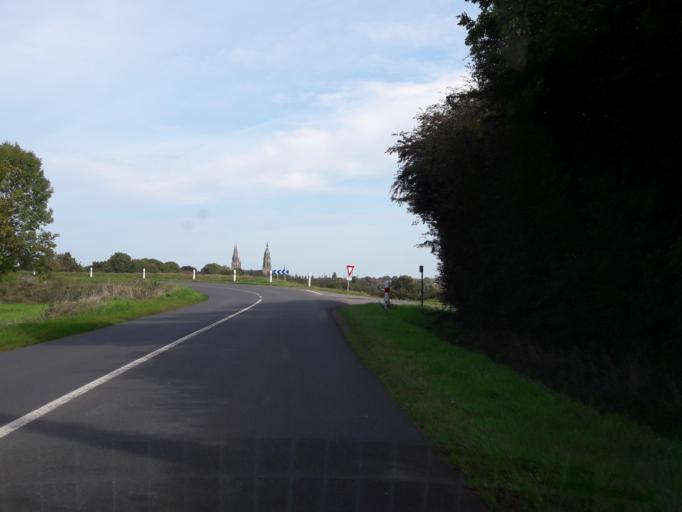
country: FR
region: Lower Normandy
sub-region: Departement du Calvados
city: Bayeux
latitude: 49.2657
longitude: -0.7095
